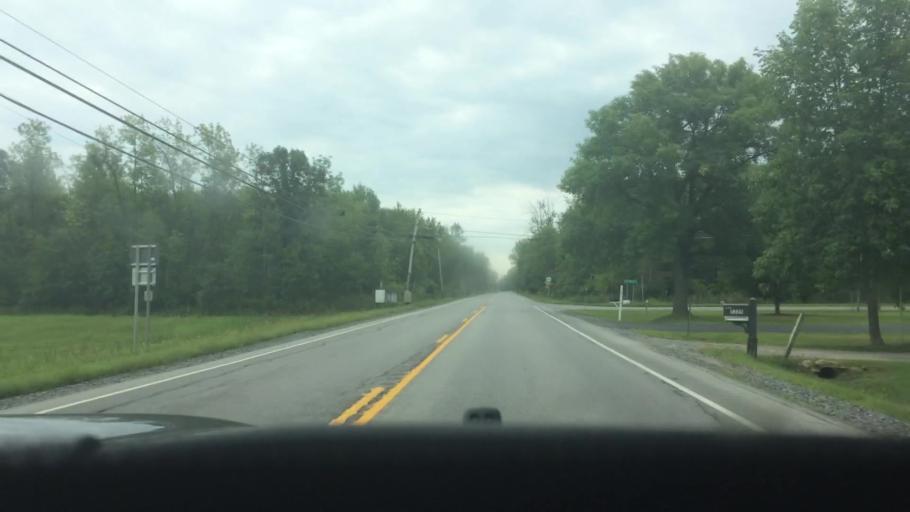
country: US
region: New York
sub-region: St. Lawrence County
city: Ogdensburg
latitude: 44.6533
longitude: -75.4458
